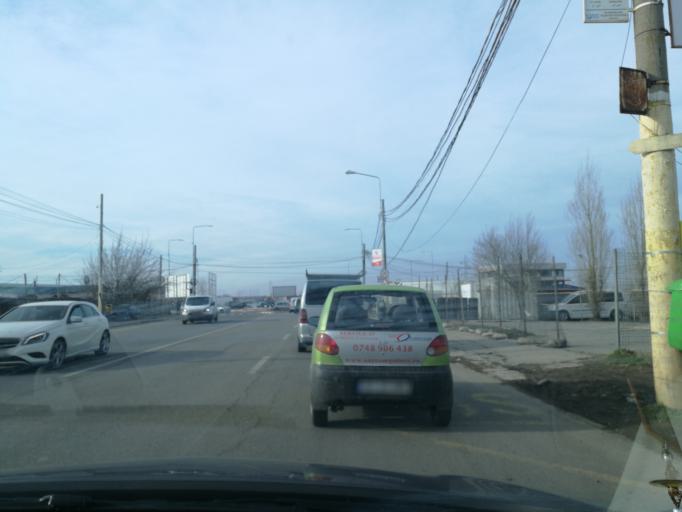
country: RO
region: Constanta
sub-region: Municipiul Constanta
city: Constanta
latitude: 44.1925
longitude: 28.6039
